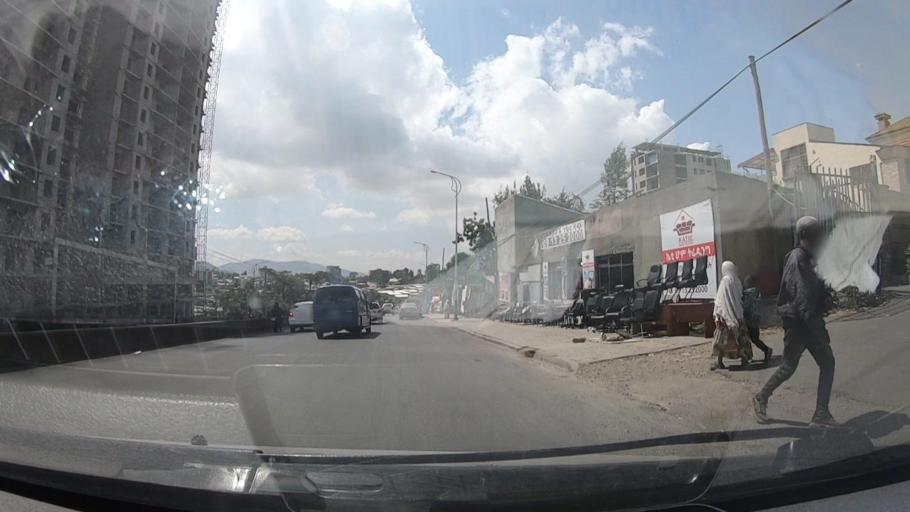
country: ET
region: Adis Abeba
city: Addis Ababa
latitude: 8.9855
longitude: 38.7206
